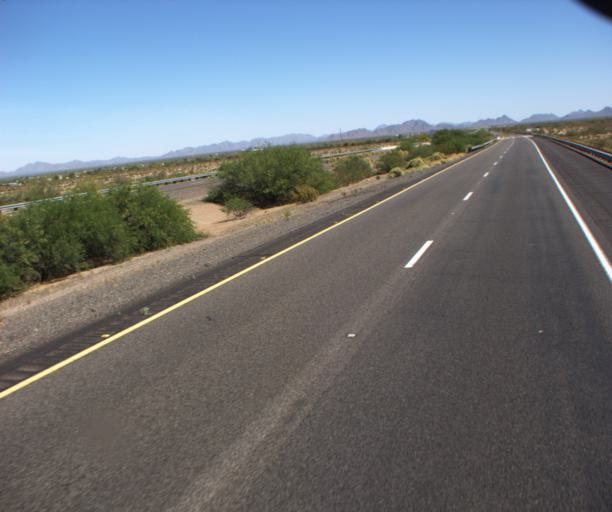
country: US
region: Arizona
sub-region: Maricopa County
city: Gila Bend
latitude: 32.9355
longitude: -112.7178
